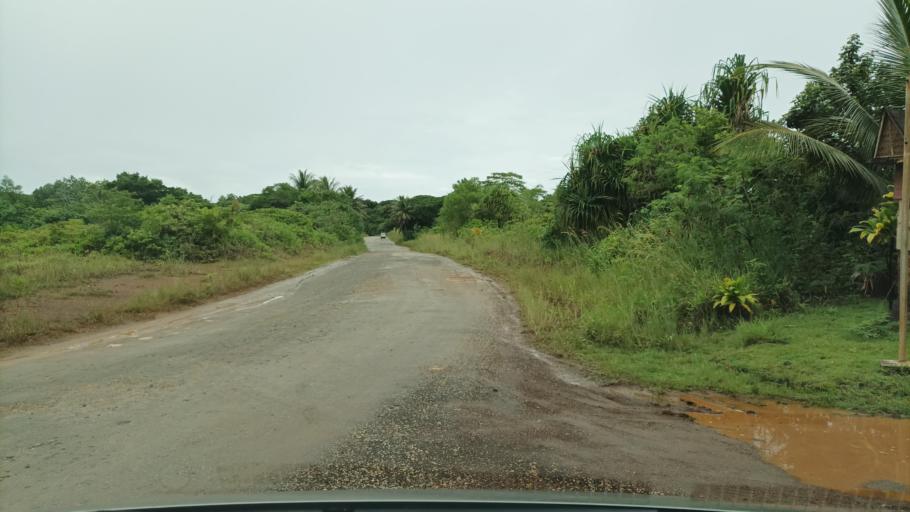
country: FM
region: Yap
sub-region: Weloy Municipality
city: Colonia
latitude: 9.5427
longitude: 138.1662
